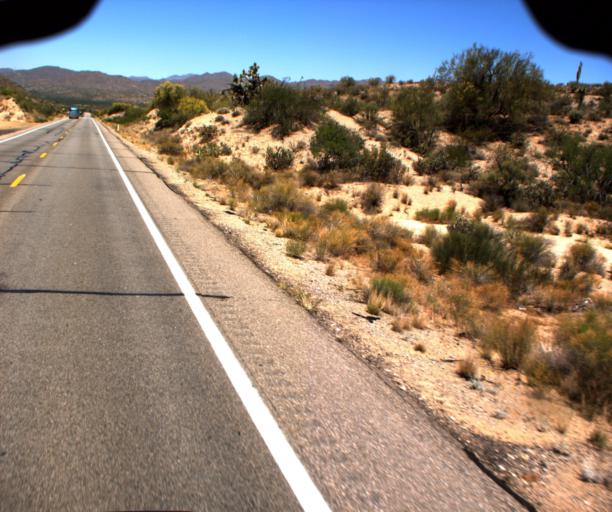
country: US
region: Arizona
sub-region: Yavapai County
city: Bagdad
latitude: 34.3554
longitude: -113.1680
